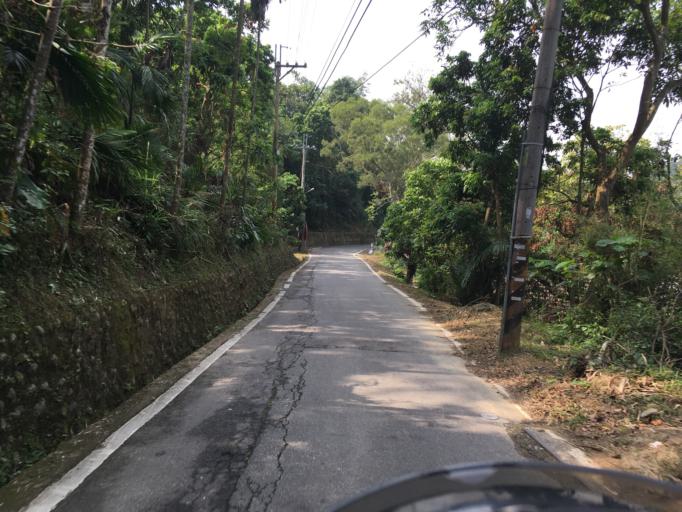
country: TW
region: Taiwan
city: Fengyuan
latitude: 24.1851
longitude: 120.7615
